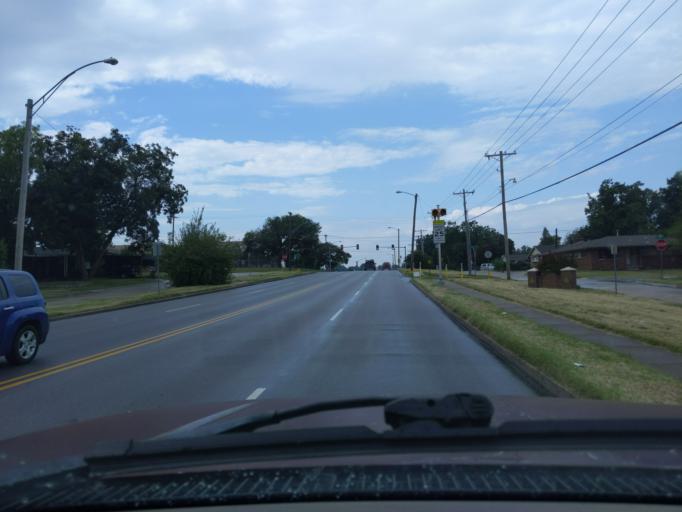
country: US
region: Oklahoma
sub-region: Tulsa County
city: Tulsa
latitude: 36.1335
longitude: -95.8945
